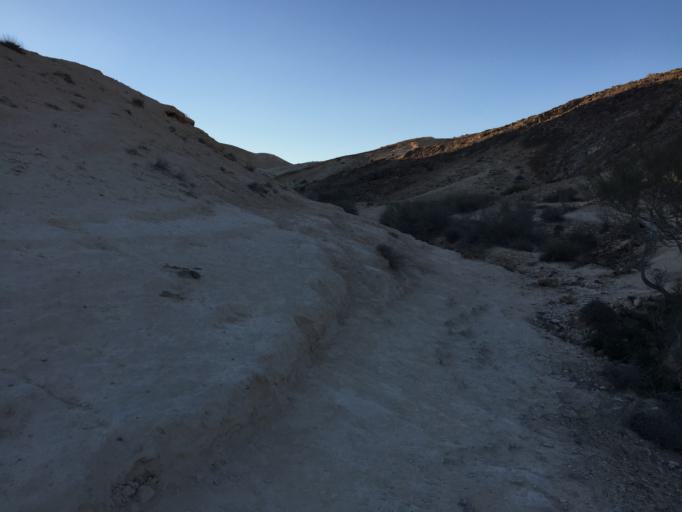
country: IL
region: Southern District
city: Midreshet Ben-Gurion
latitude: 30.8439
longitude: 34.7586
